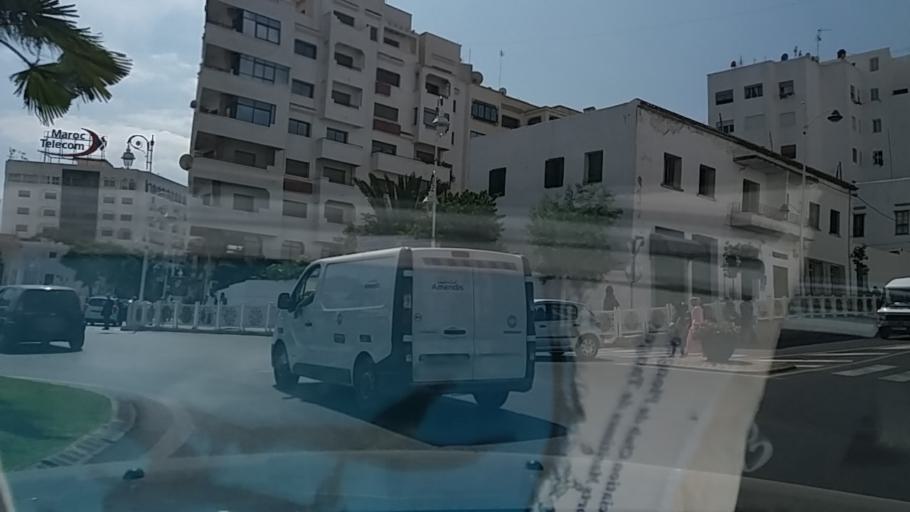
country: MA
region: Tanger-Tetouan
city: Tetouan
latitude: 35.5718
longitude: -5.3597
